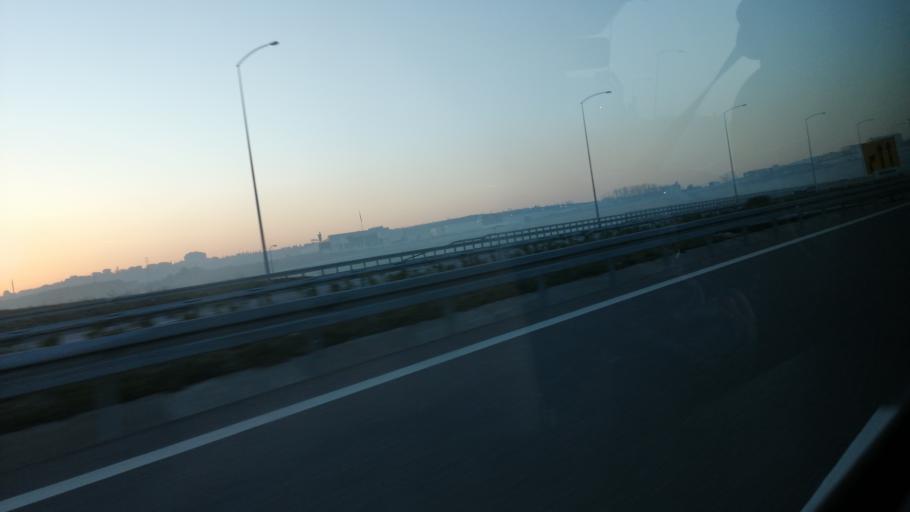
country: TR
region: Kocaeli
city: Tavsanli
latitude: 40.7943
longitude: 29.5111
